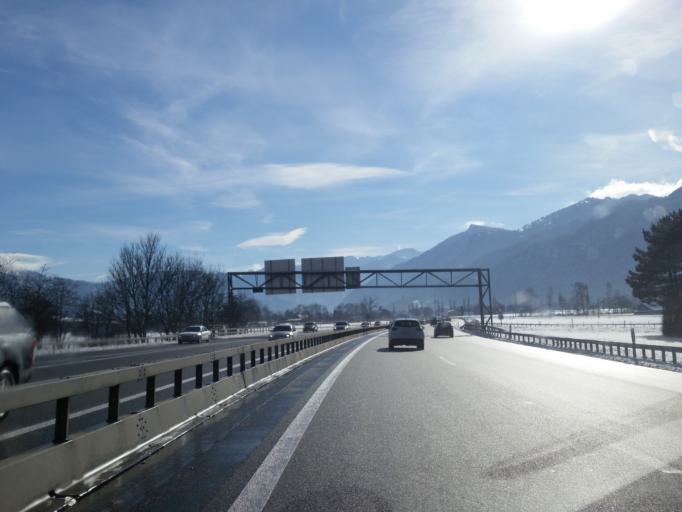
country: CH
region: Saint Gallen
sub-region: Wahlkreis Sarganserland
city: Sargans
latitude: 47.0361
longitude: 9.4640
